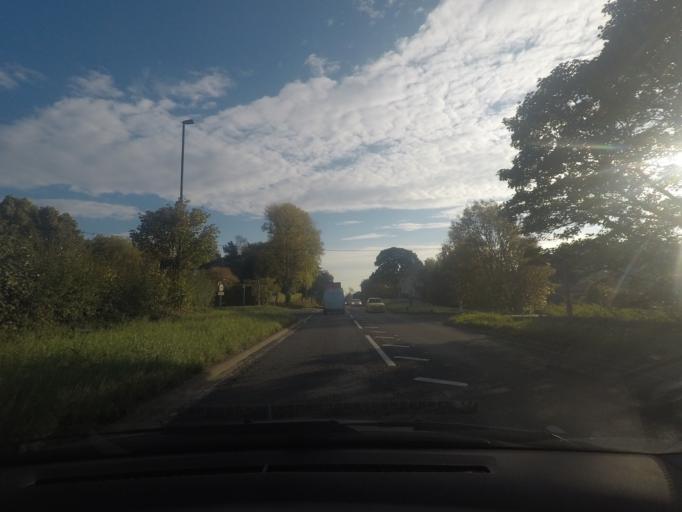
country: GB
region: England
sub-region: City of York
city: Murton
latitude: 53.9572
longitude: -1.0052
